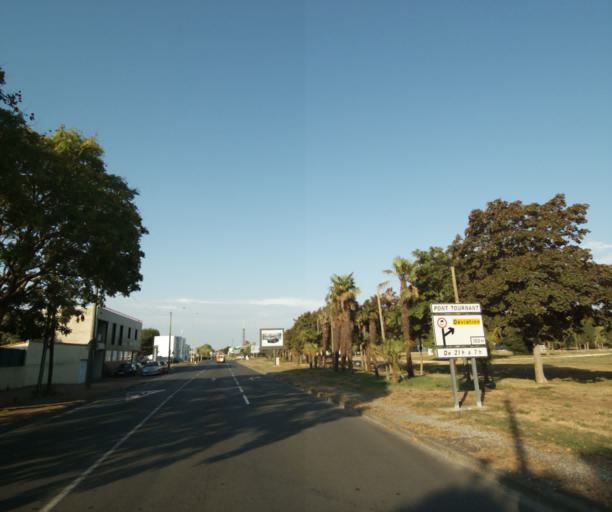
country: FR
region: Poitou-Charentes
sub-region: Departement de la Charente-Maritime
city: Breuil-Magne
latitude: 45.9510
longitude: -0.9435
